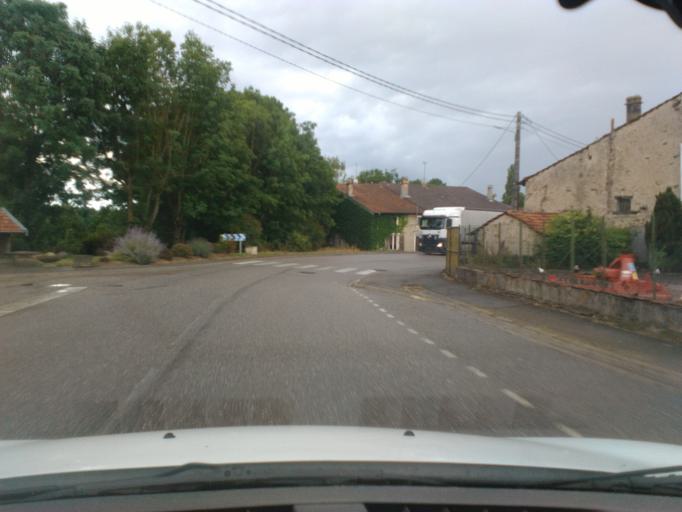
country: FR
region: Lorraine
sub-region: Departement des Vosges
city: Mirecourt
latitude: 48.3970
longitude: 6.1358
